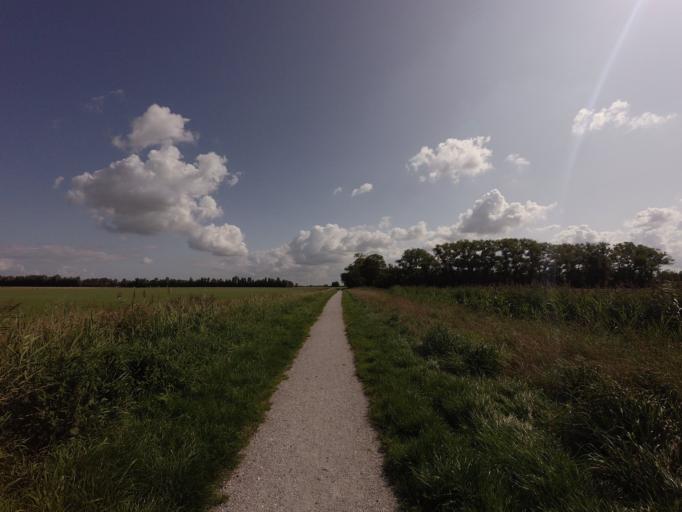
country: NL
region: Friesland
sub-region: Gemeente Het Bildt
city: Sint Annaparochie
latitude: 53.2797
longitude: 5.6660
